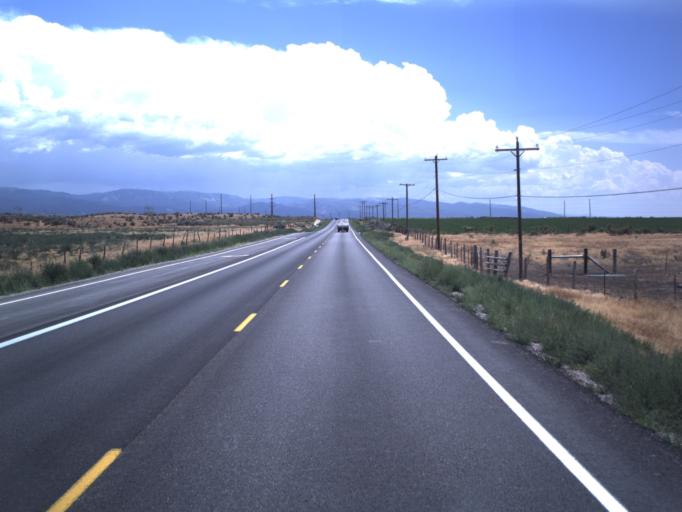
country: US
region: Utah
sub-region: Sanpete County
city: Moroni
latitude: 39.5568
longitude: -111.6007
